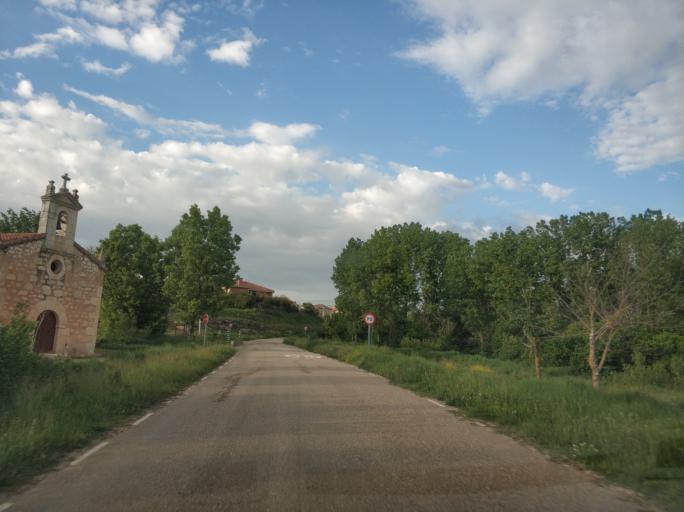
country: ES
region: Castille and Leon
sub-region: Provincia de Burgos
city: Brazacorta
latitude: 41.7150
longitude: -3.3691
